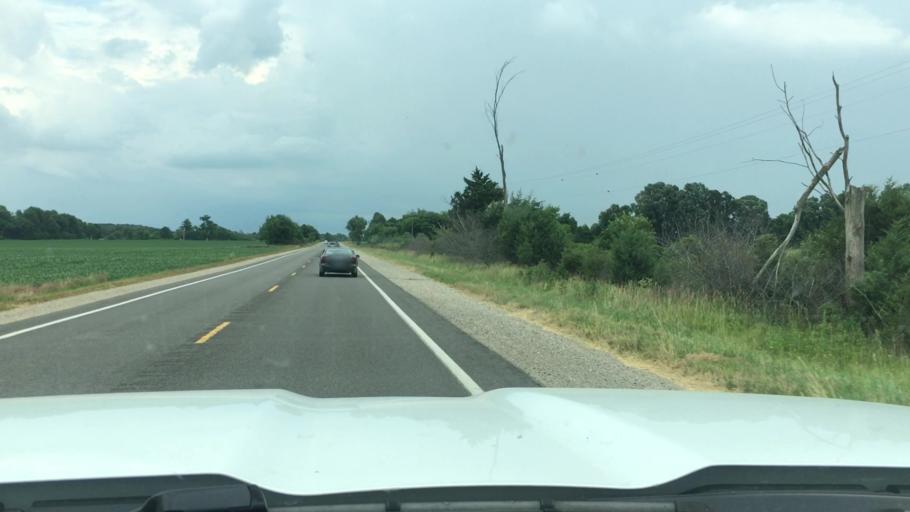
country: US
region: Michigan
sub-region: Montcalm County
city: Stanton
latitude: 43.1782
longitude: -85.0626
